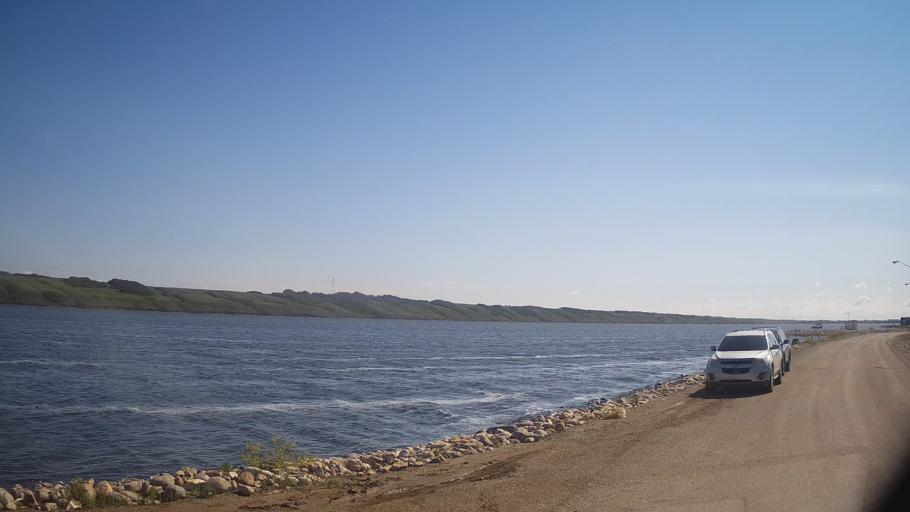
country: CA
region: Saskatchewan
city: Watrous
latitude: 51.7221
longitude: -105.4550
